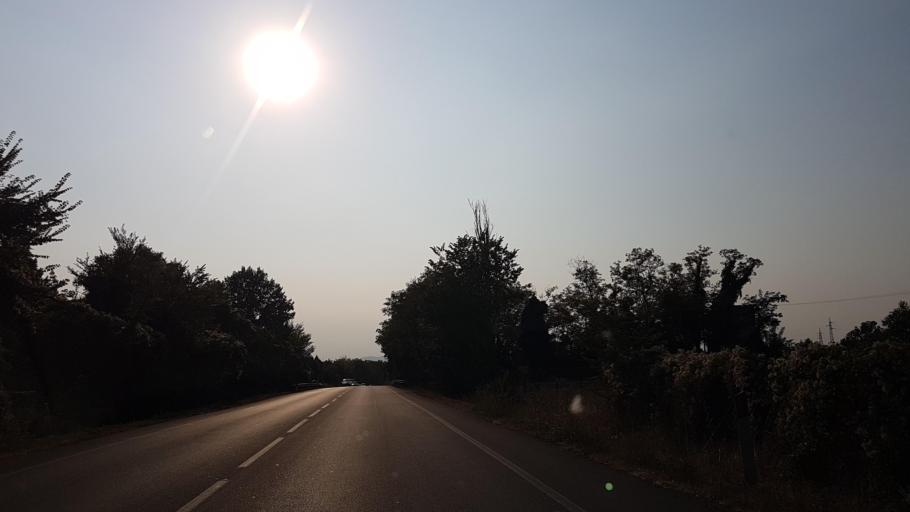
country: IT
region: Emilia-Romagna
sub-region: Provincia di Parma
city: Collecchio
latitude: 44.7580
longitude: 10.2218
